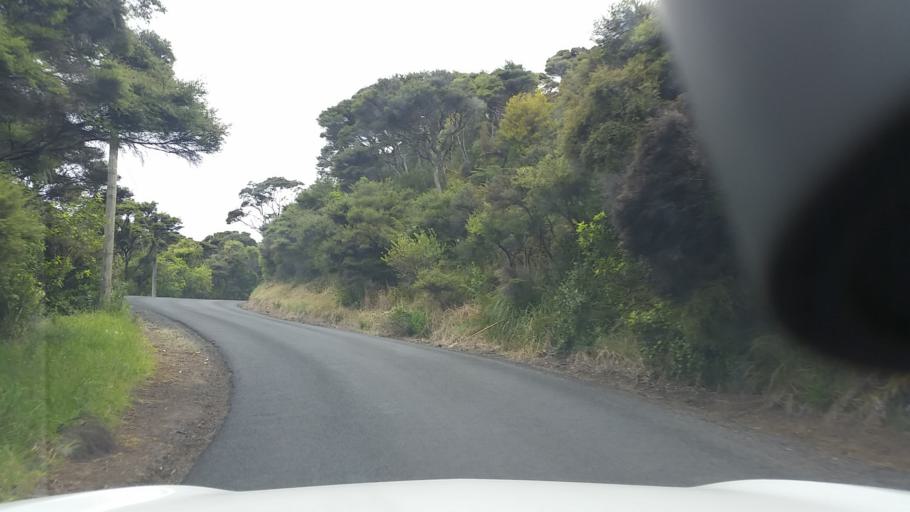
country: NZ
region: Auckland
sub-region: Auckland
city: Muriwai Beach
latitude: -36.8760
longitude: 174.4648
